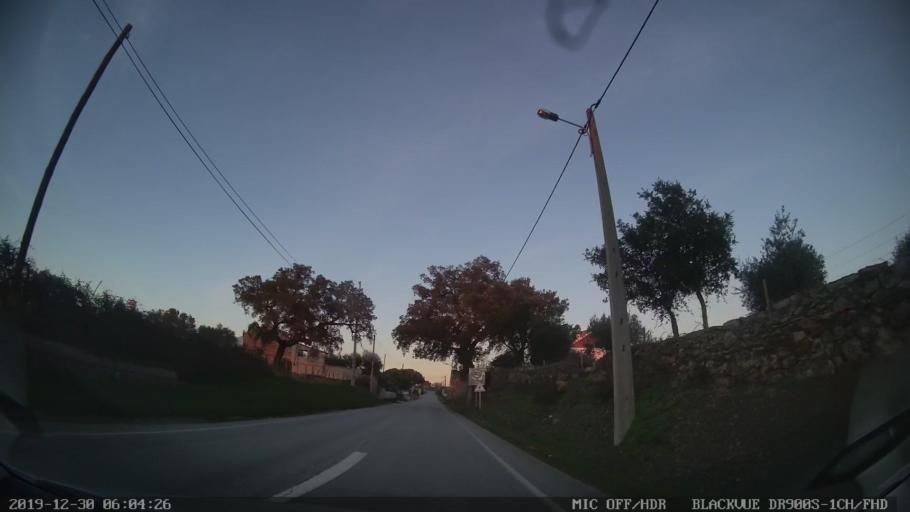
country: PT
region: Castelo Branco
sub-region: Penamacor
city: Penamacor
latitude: 40.0842
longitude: -7.2382
